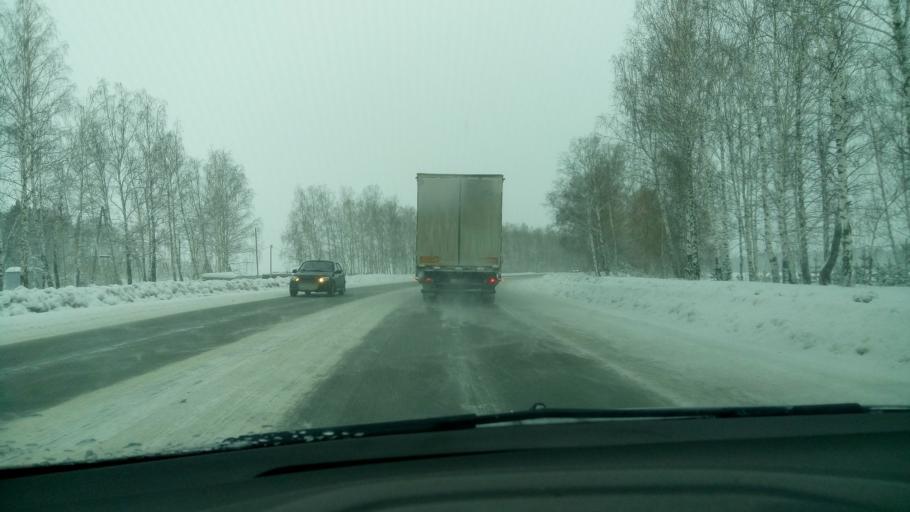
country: RU
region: Sverdlovsk
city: Zarechnyy
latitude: 56.7482
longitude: 61.3090
